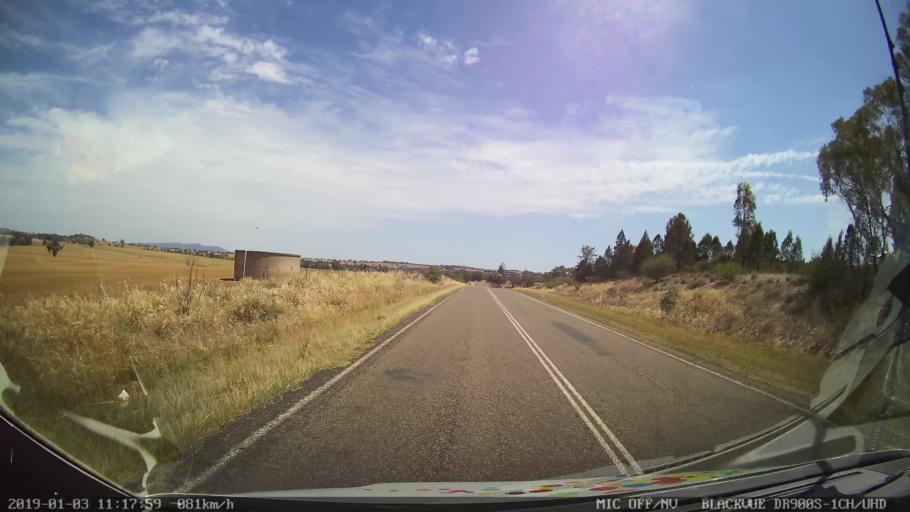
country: AU
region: New South Wales
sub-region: Young
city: Young
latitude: -34.1314
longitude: 148.2636
